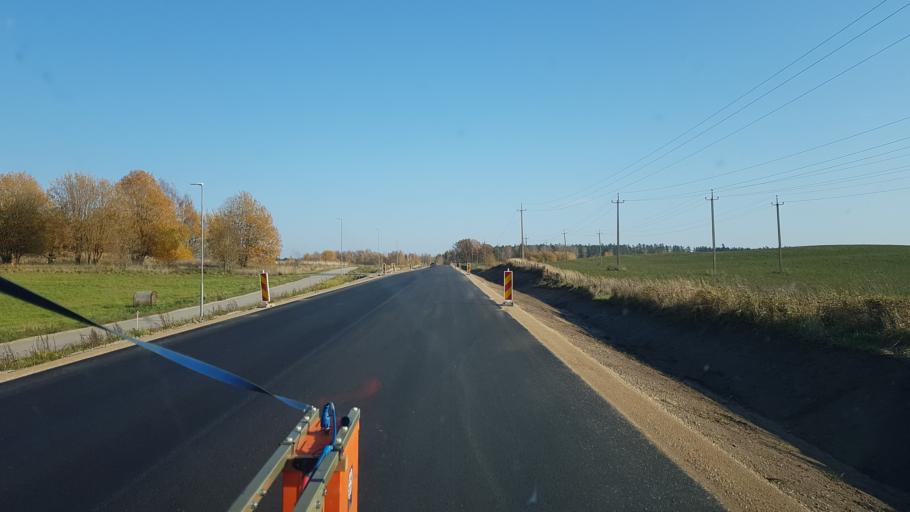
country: EE
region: Vorumaa
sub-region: Antsla vald
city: Vana-Antsla
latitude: 57.8388
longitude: 26.4911
